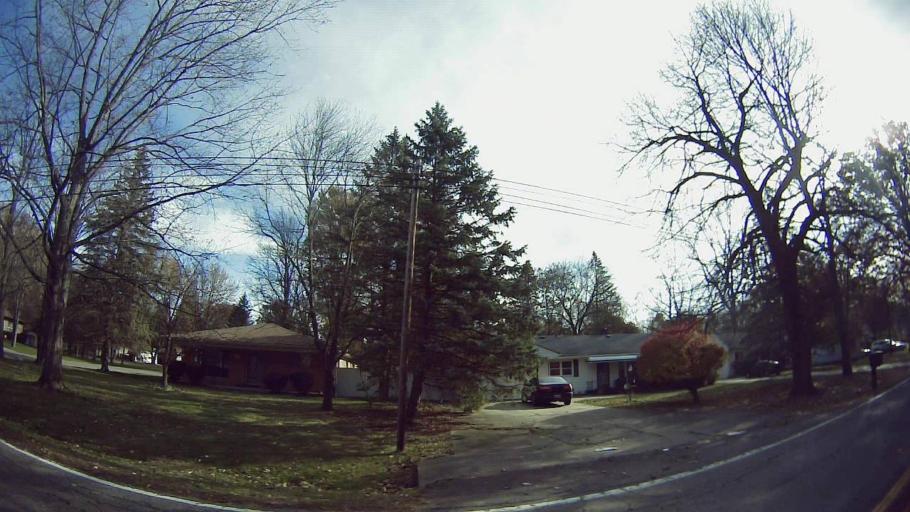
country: US
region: Michigan
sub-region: Oakland County
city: Southfield
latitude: 42.4481
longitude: -83.2701
